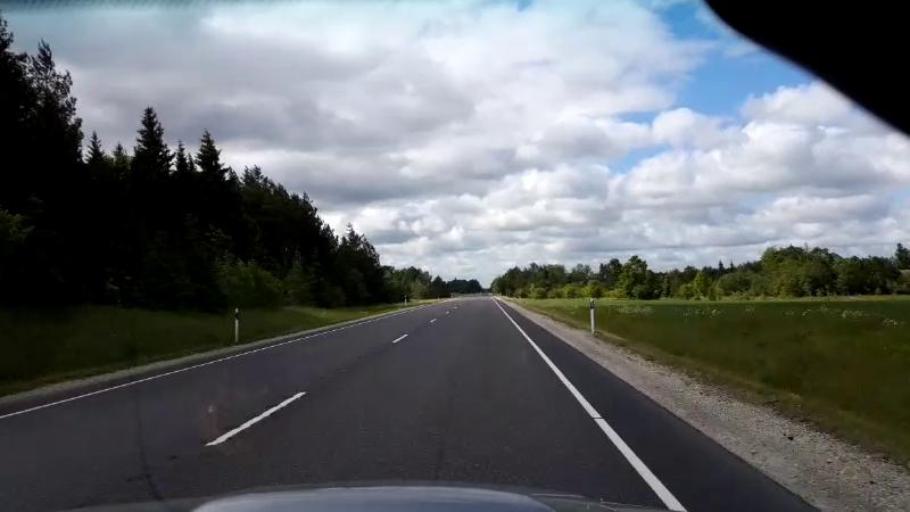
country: EE
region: Raplamaa
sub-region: Maerjamaa vald
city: Marjamaa
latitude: 58.8634
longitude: 24.4379
